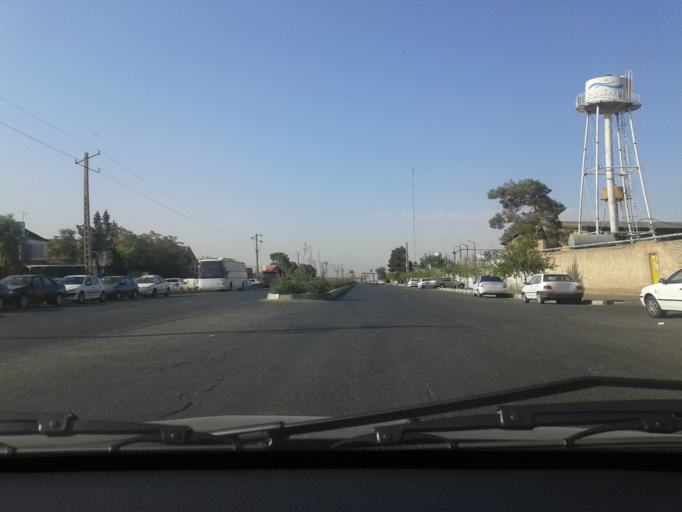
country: IR
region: Tehran
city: Shahr-e Qods
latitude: 35.7024
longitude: 51.2328
